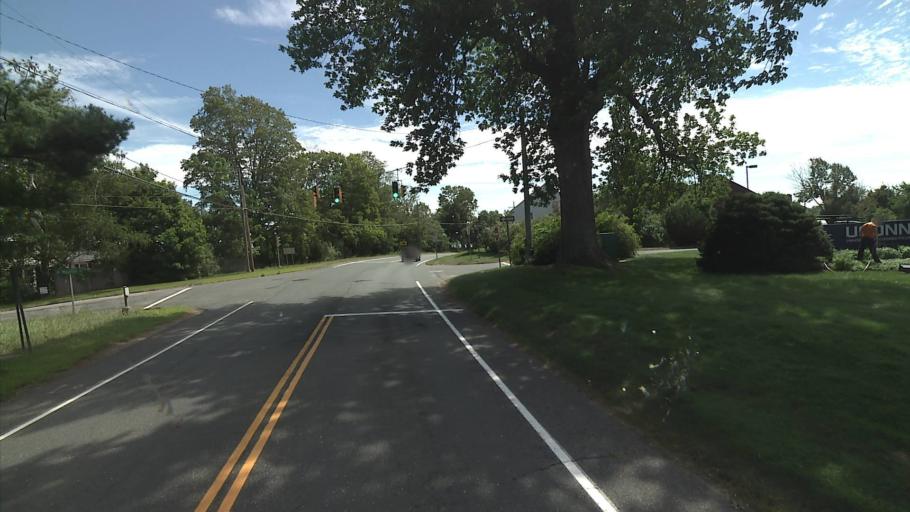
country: US
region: Connecticut
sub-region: Tolland County
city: Storrs
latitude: 41.8190
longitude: -72.2557
